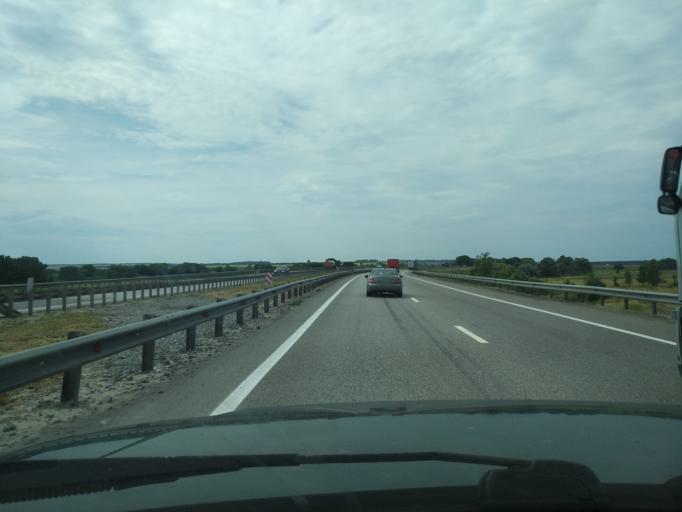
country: RU
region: Lipetsk
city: Khlevnoye
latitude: 52.0587
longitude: 39.1863
